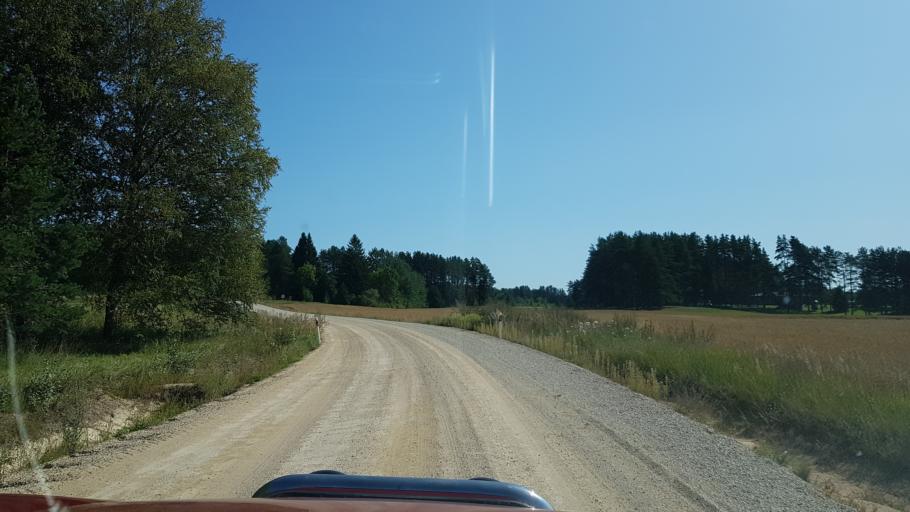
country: EE
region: Vorumaa
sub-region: Voru linn
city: Voru
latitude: 57.7353
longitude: 27.2607
